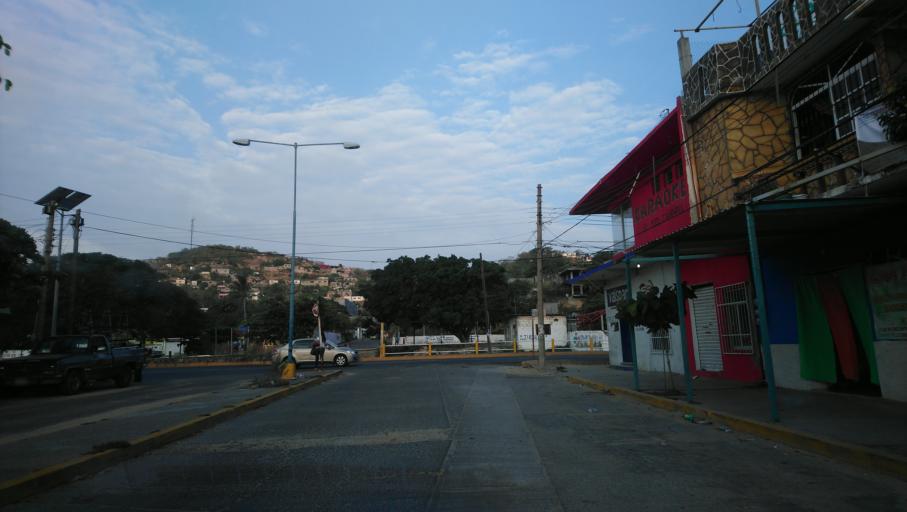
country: MX
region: Oaxaca
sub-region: Salina Cruz
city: Salina Cruz
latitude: 16.1834
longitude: -95.1990
